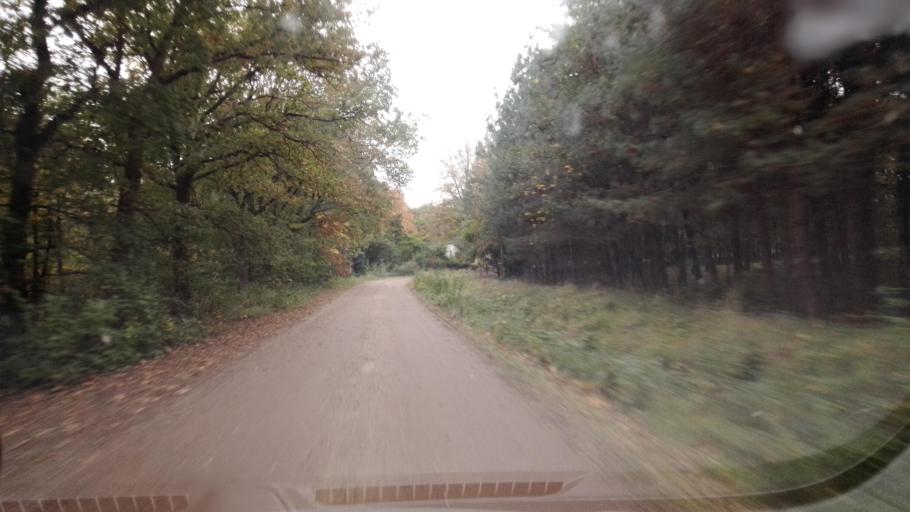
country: NL
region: Limburg
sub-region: Gemeente Venlo
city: Venlo
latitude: 51.3979
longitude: 6.1225
